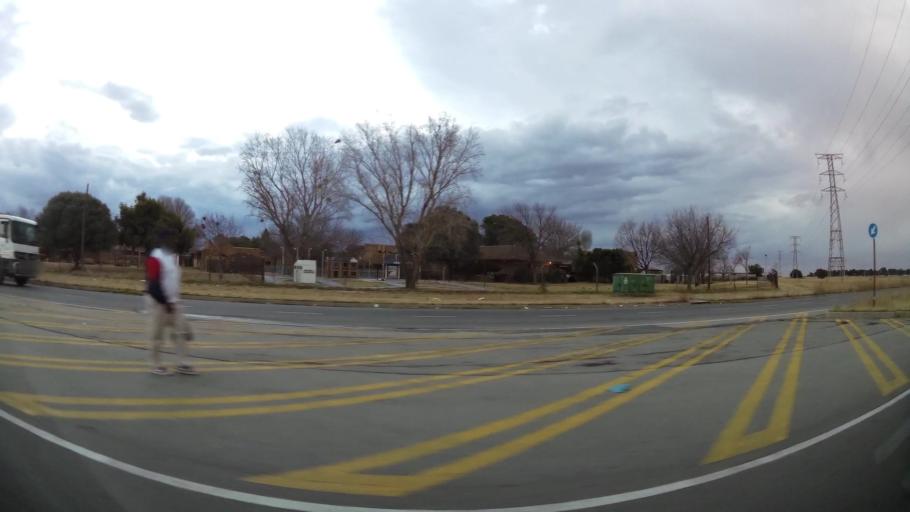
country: ZA
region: Orange Free State
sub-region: Lejweleputswa District Municipality
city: Welkom
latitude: -27.9530
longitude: 26.7561
